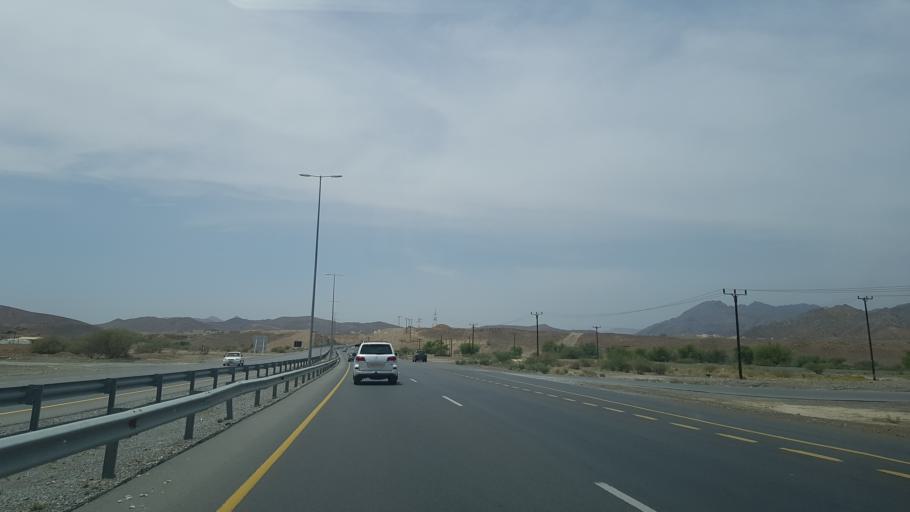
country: OM
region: Muhafazat ad Dakhiliyah
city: Izki
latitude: 22.9139
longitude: 57.7670
